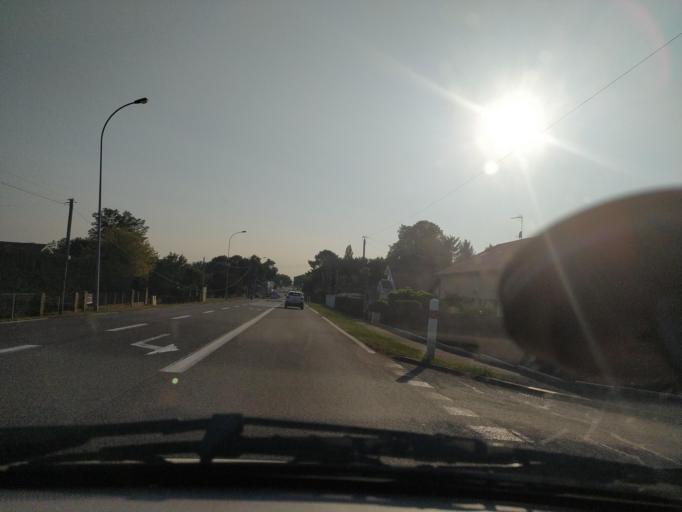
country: FR
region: Aquitaine
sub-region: Departement des Landes
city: Saint-Geours-de-Maremne
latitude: 43.6856
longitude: -1.2349
